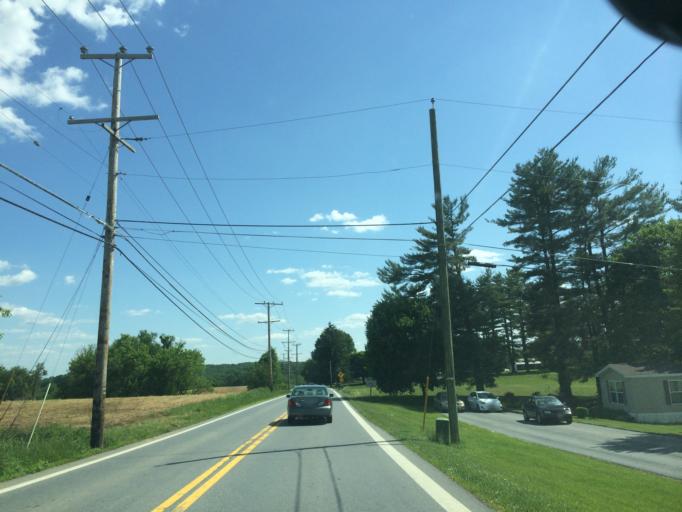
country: US
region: Maryland
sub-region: Carroll County
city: Eldersburg
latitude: 39.4482
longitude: -76.9249
